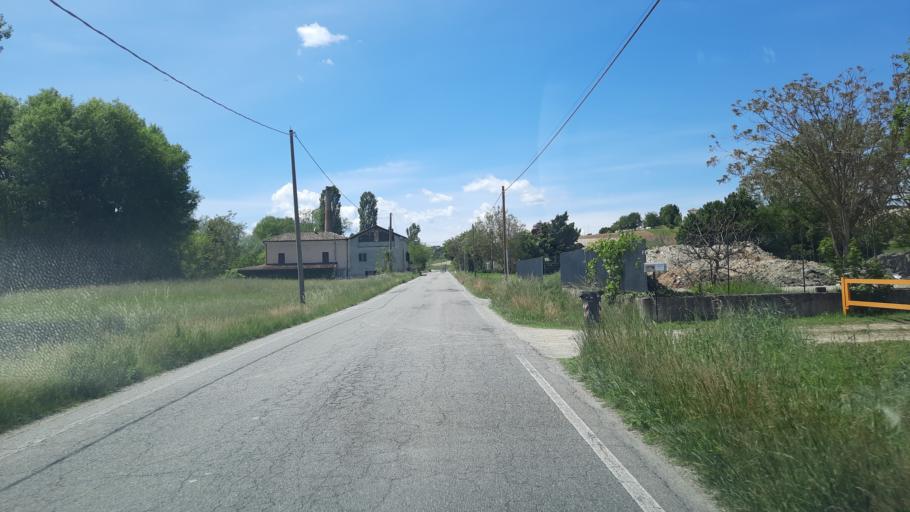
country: IT
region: Piedmont
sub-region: Provincia di Asti
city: Moncalvo
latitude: 45.0617
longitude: 8.2572
